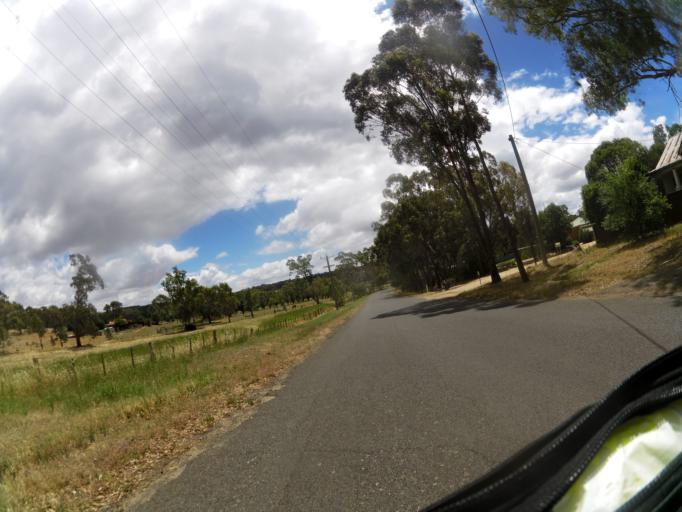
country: AU
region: Victoria
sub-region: Mount Alexander
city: Castlemaine
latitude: -37.0147
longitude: 144.2517
